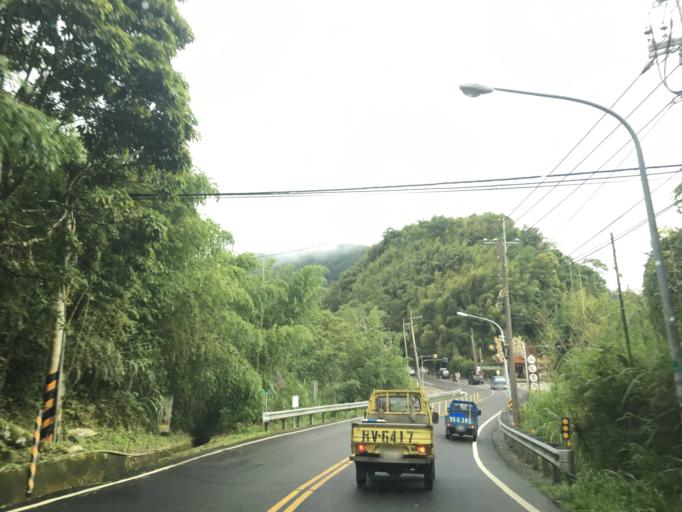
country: TW
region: Taiwan
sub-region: Chiayi
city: Jiayi Shi
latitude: 23.4563
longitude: 120.6839
